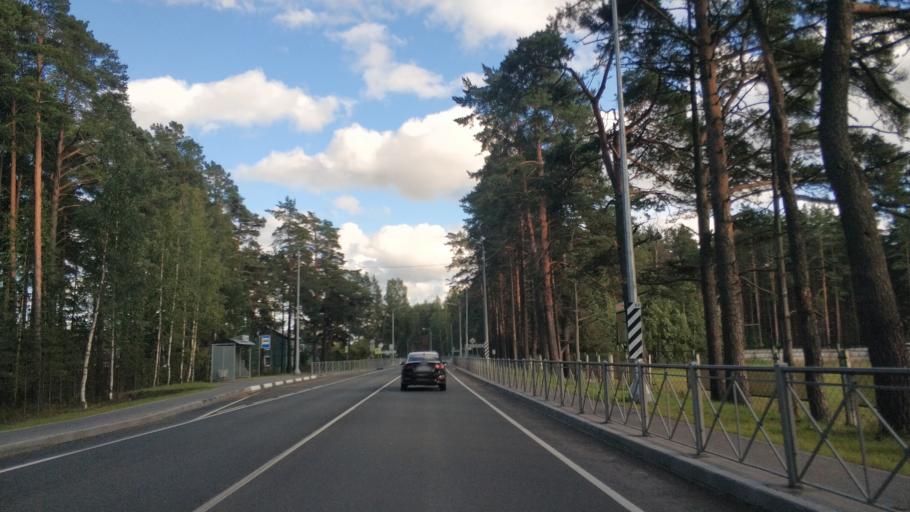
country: RU
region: Leningrad
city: Priozersk
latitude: 61.0184
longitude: 30.1368
